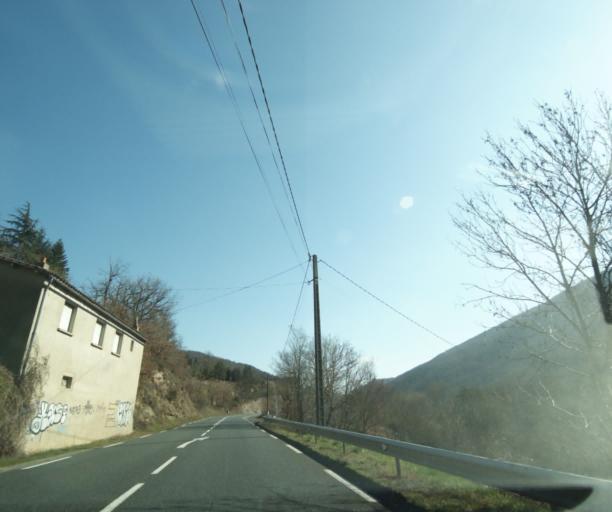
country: FR
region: Midi-Pyrenees
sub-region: Departement de l'Aveyron
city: Saint-Affrique
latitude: 43.9545
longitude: 2.9261
